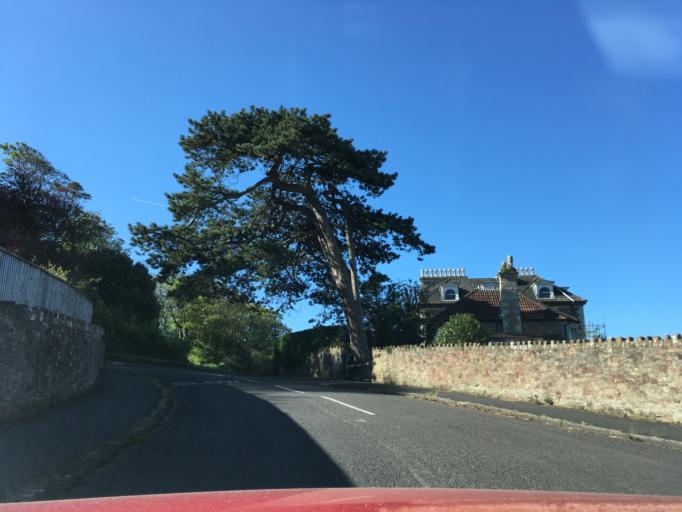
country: GB
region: England
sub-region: North Somerset
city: Portishead
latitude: 51.4926
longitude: -2.7687
